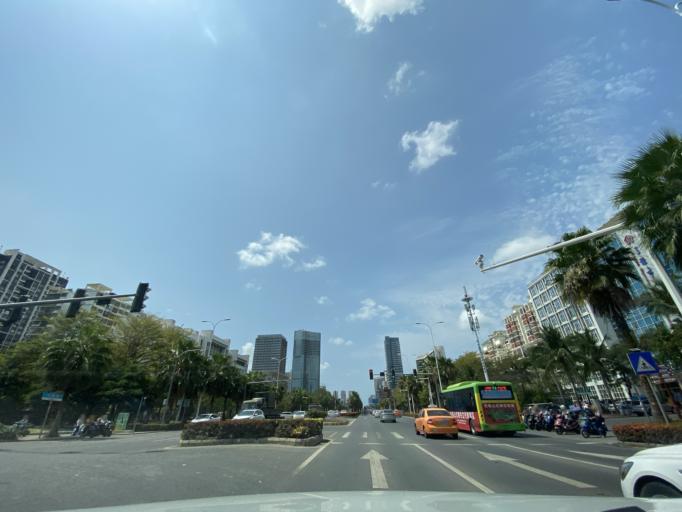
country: CN
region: Hainan
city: Sanya
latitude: 18.2801
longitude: 109.5125
